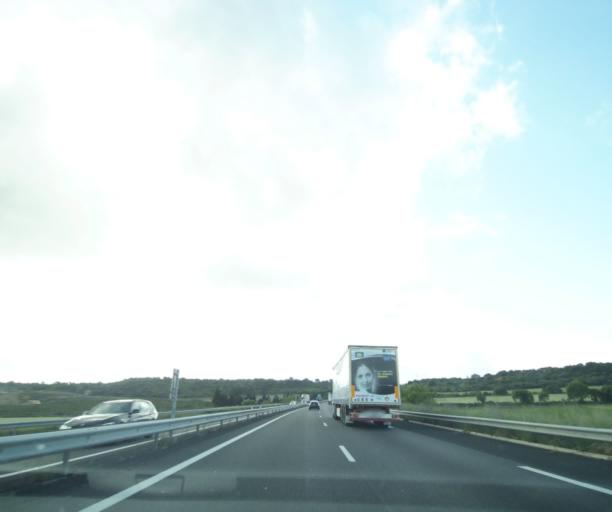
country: FR
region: Languedoc-Roussillon
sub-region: Departement du Gard
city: Bellegarde
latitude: 43.7334
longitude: 4.4694
